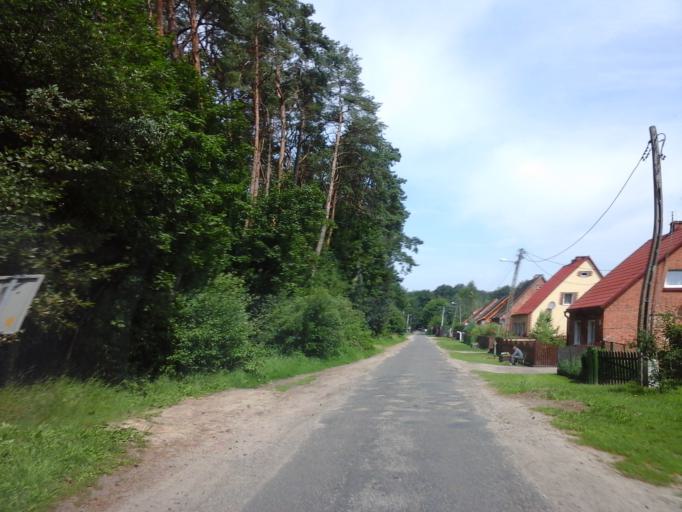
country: PL
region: West Pomeranian Voivodeship
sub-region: Powiat choszczenski
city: Bierzwnik
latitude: 53.0092
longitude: 15.6377
